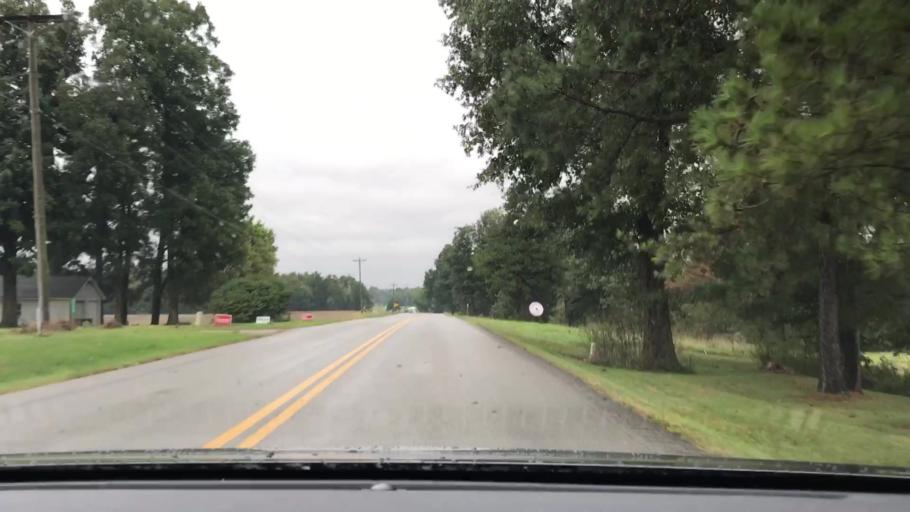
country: US
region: Kentucky
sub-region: McLean County
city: Calhoun
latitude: 37.4606
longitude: -87.2338
